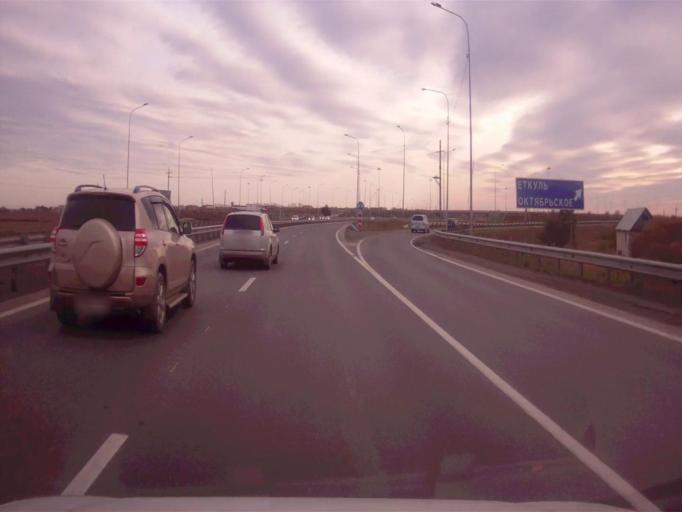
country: RU
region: Chelyabinsk
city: Novosineglazovskiy
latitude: 55.0071
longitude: 61.4528
